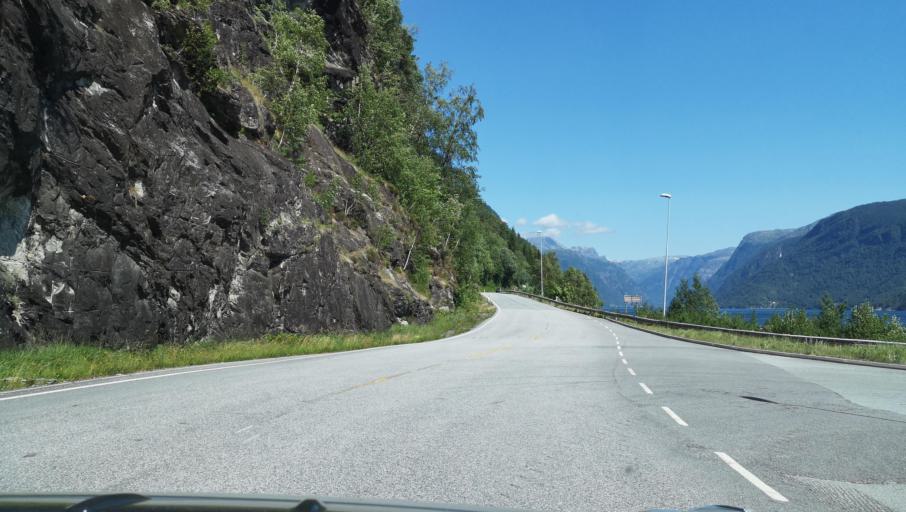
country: NO
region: Hordaland
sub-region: Ulvik
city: Ulvik
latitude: 60.4937
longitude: 6.8919
